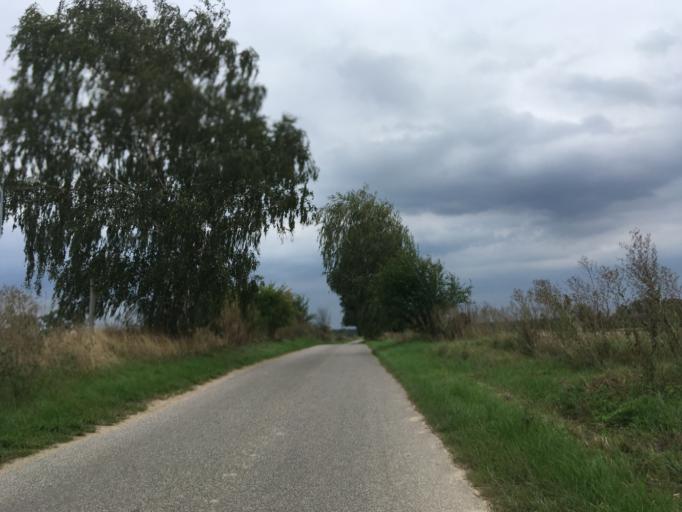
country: DE
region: Brandenburg
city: Joachimsthal
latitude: 53.0238
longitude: 13.7708
